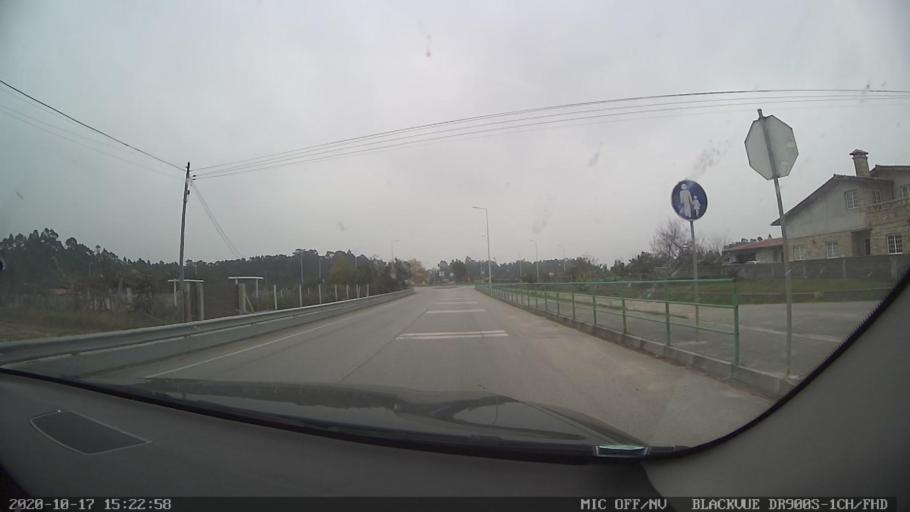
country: PT
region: Braga
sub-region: Esposende
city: Esposende
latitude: 41.5310
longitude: -8.7372
